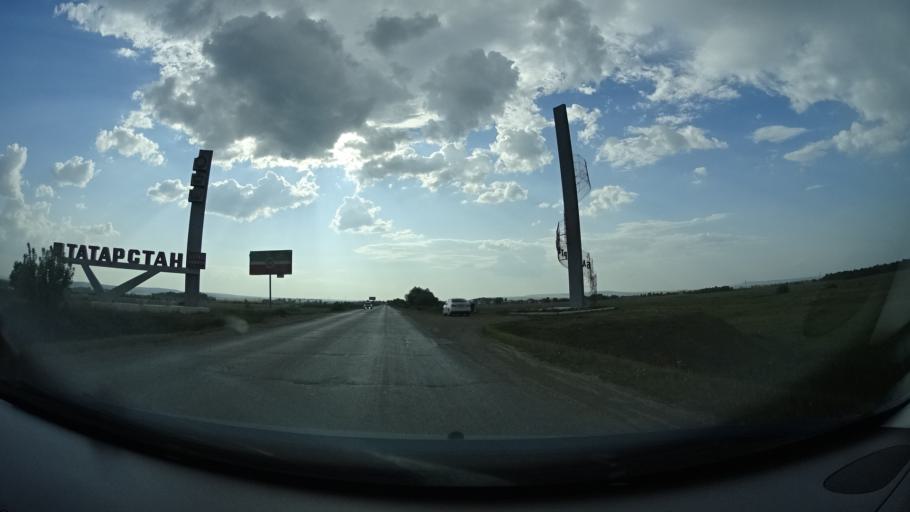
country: RU
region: Bashkortostan
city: Oktyabr'skiy
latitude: 54.4858
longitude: 53.4272
